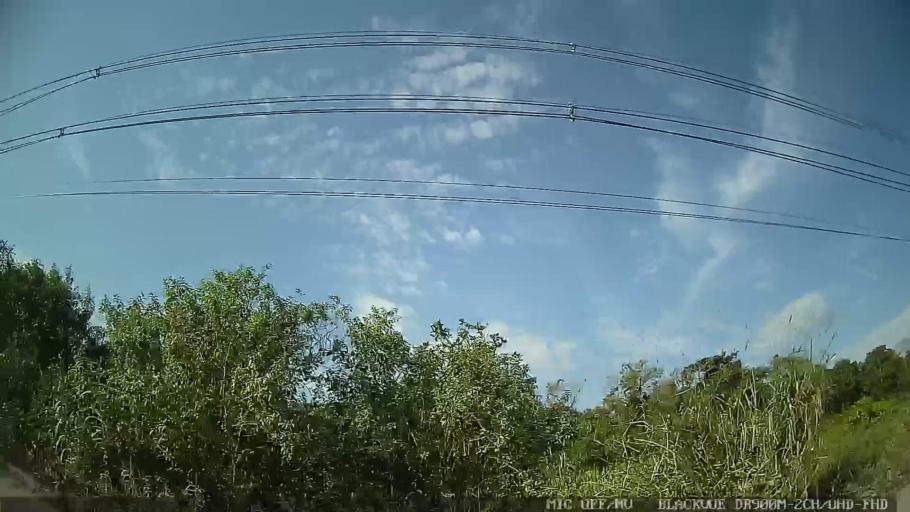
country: BR
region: Sao Paulo
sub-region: Guaruja
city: Guaruja
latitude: -23.9590
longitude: -46.2738
